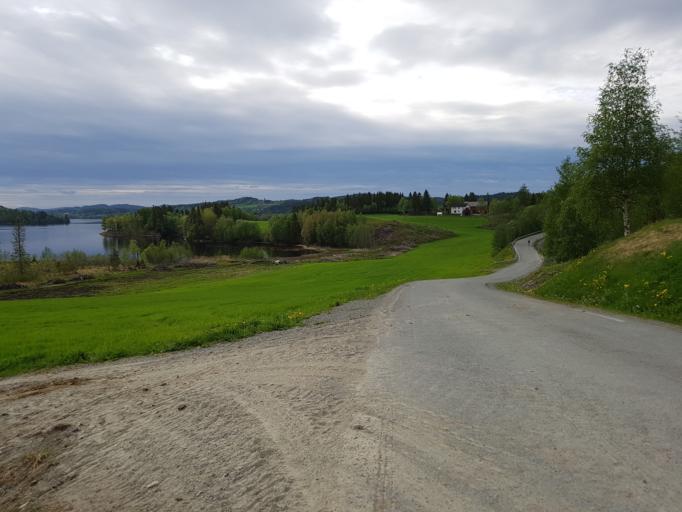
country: NO
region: Nord-Trondelag
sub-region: Levanger
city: Skogn
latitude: 63.6237
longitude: 11.2770
